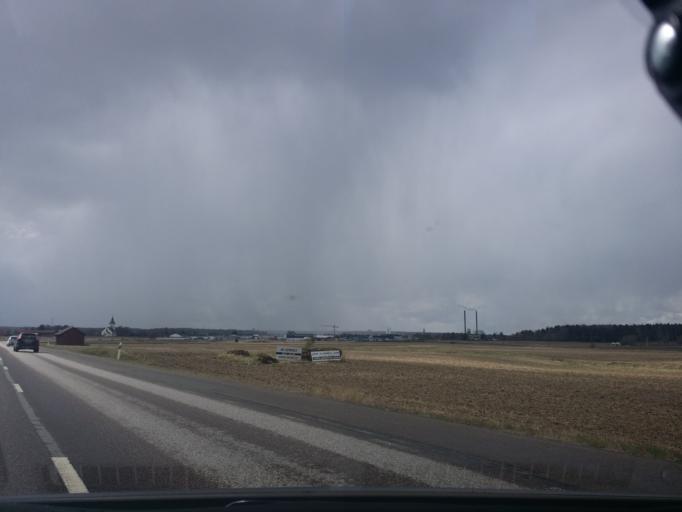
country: SE
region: Vaestmanland
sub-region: Sala Kommun
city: Sala
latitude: 59.9193
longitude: 16.6474
